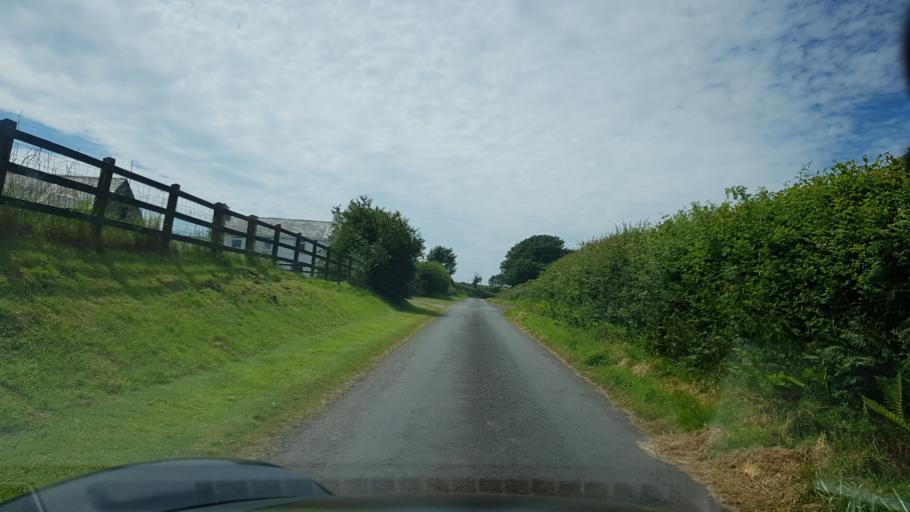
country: GB
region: Wales
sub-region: Carmarthenshire
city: Llanddowror
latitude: 51.7684
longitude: -4.4988
